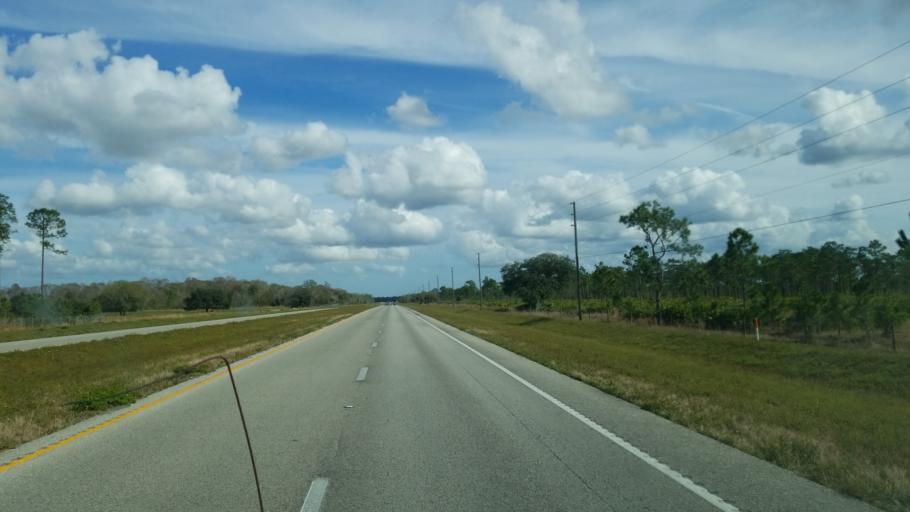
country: US
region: Florida
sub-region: Osceola County
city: Saint Cloud
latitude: 28.1368
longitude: -81.0345
